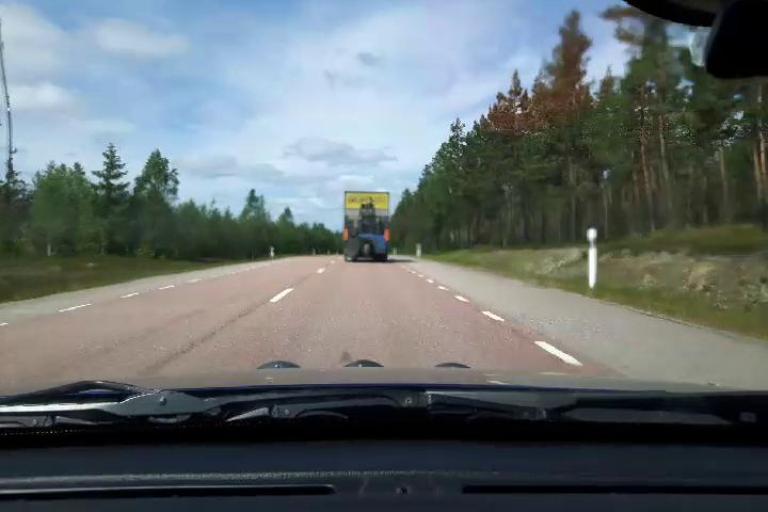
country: SE
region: Uppsala
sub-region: Osthammars Kommun
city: Bjorklinge
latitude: 60.1776
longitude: 17.4826
